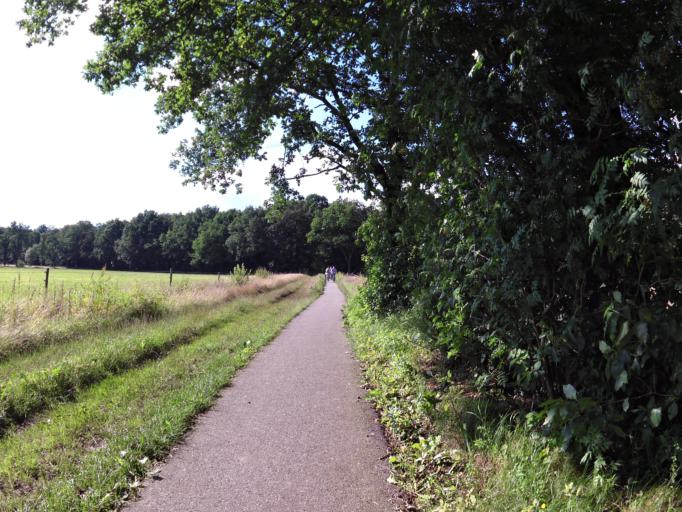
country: NL
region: North Brabant
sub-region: Gemeente Geldrop-Mierlo
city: Geldrop
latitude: 51.4020
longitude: 5.5460
